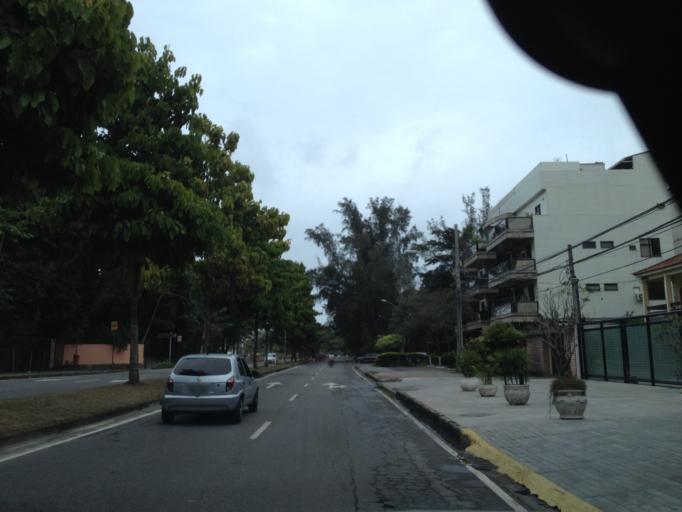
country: BR
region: Rio de Janeiro
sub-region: Nilopolis
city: Nilopolis
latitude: -23.0166
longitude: -43.4491
